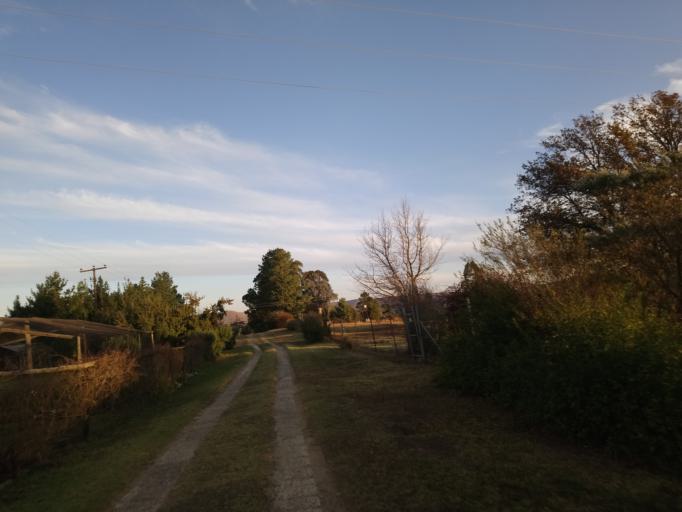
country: ZA
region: KwaZulu-Natal
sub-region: uMgungundlovu District Municipality
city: Mooirivier
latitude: -29.3318
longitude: 29.9194
